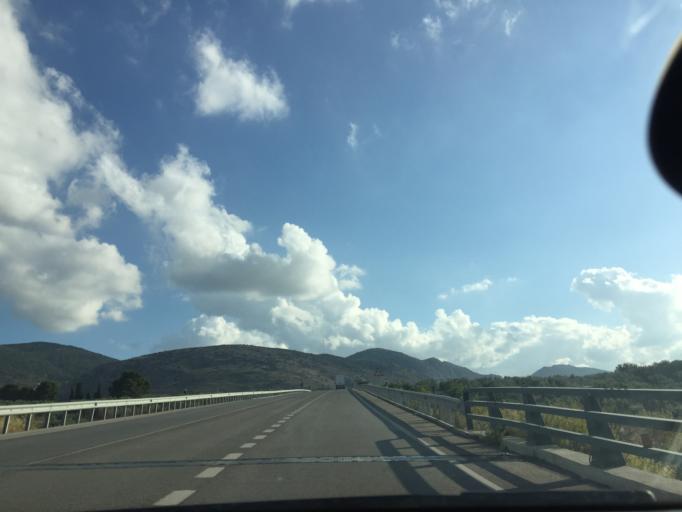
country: ES
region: Andalusia
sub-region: Provincia de Jaen
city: Mancha Real
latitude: 37.7927
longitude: -3.6223
